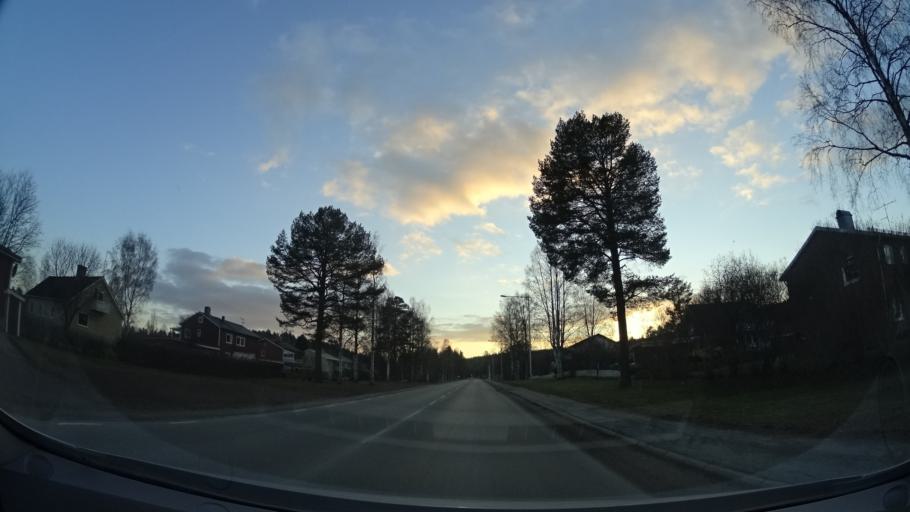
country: SE
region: Vaesterbotten
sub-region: Lycksele Kommun
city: Lycksele
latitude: 64.5874
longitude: 18.6654
